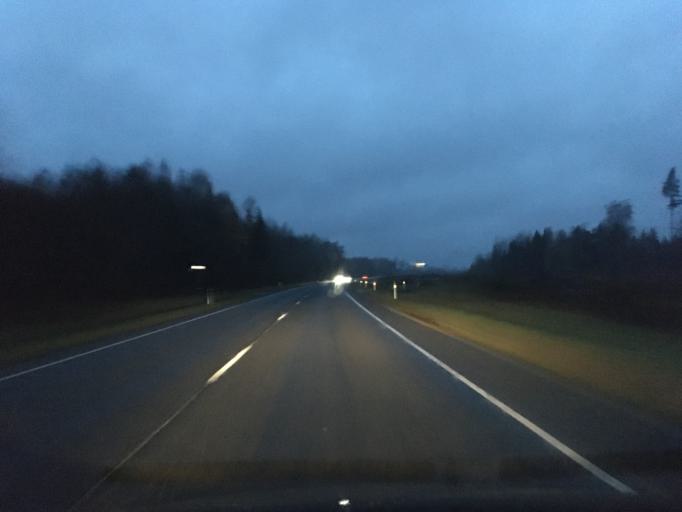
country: EE
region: Harju
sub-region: Nissi vald
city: Turba
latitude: 58.9713
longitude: 24.0631
